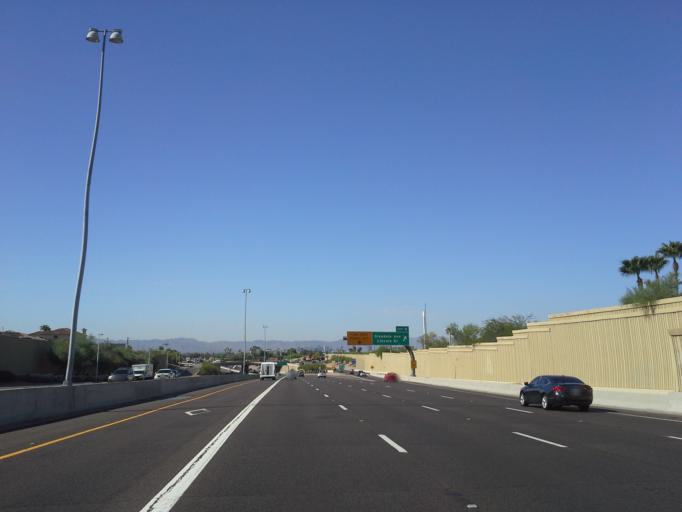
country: US
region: Arizona
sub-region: Maricopa County
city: Paradise Valley
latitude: 33.5429
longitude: -112.0406
